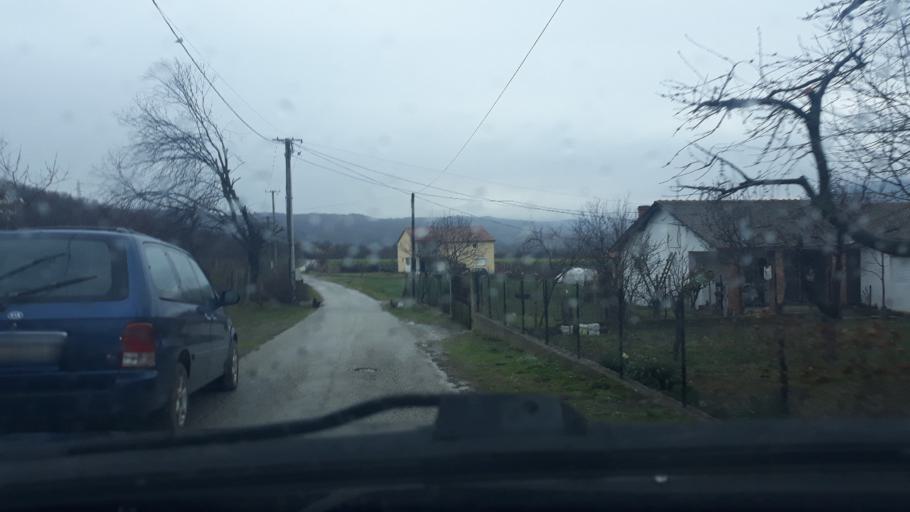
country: MK
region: Bogdanci
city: Bogdanci
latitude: 41.2364
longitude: 22.6525
